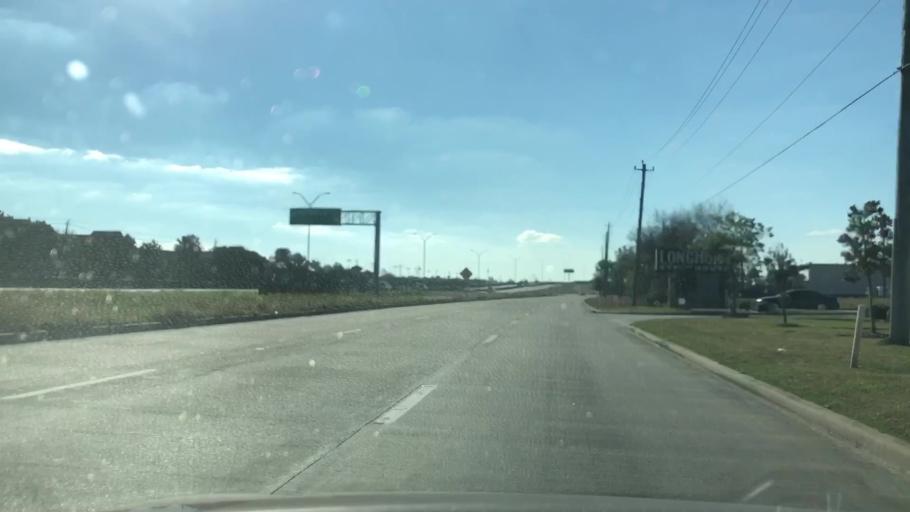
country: US
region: Texas
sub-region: Harris County
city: Cloverleaf
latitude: 29.8152
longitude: -95.1648
